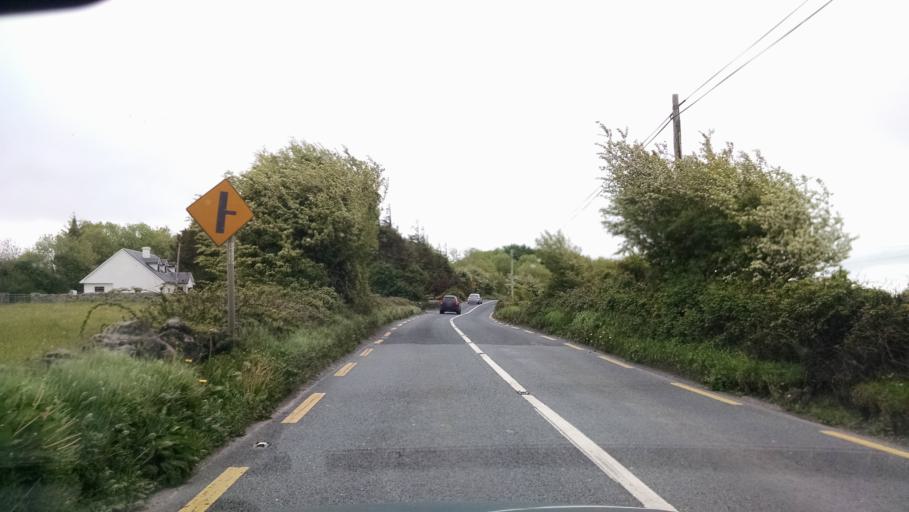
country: IE
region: Connaught
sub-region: County Galway
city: Claregalway
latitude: 53.4278
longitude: -9.0549
